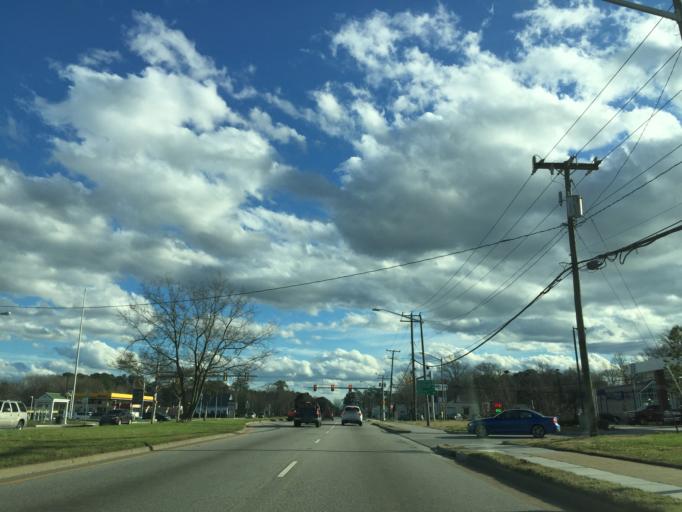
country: US
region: Virginia
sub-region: York County
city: Yorktown
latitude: 37.1147
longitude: -76.5198
